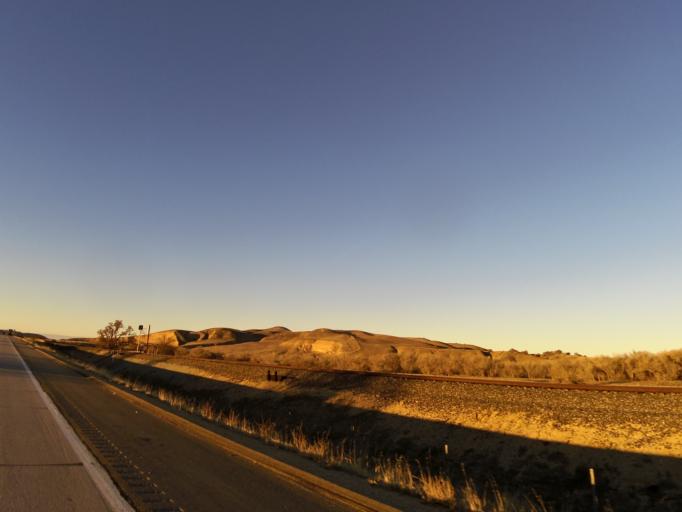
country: US
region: California
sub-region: San Luis Obispo County
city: San Miguel
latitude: 35.7877
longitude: -120.7289
